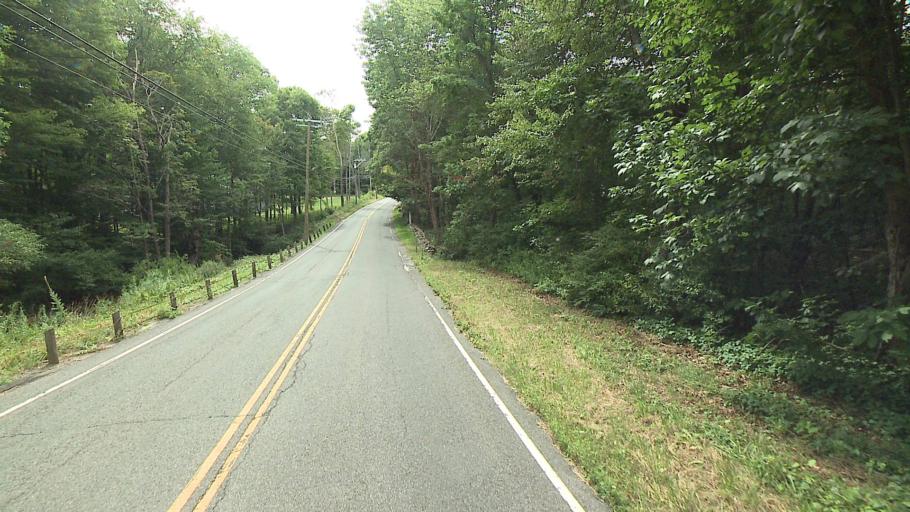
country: US
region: Connecticut
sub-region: Litchfield County
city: New Preston
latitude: 41.6124
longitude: -73.2900
